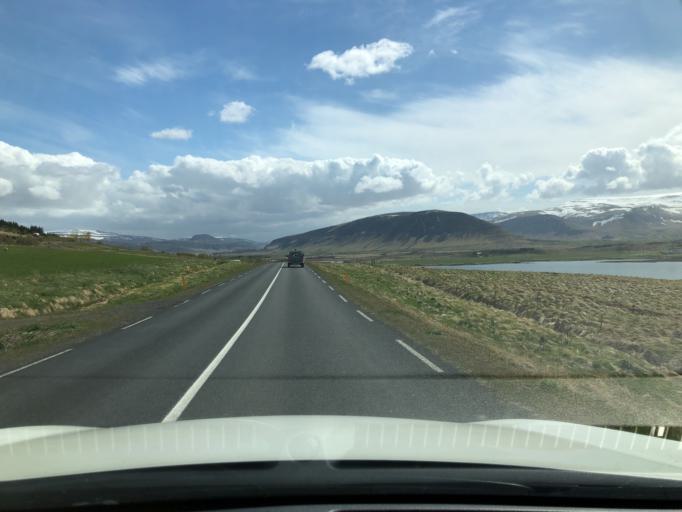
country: IS
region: Capital Region
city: Mosfellsbaer
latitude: 64.3528
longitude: -21.6383
